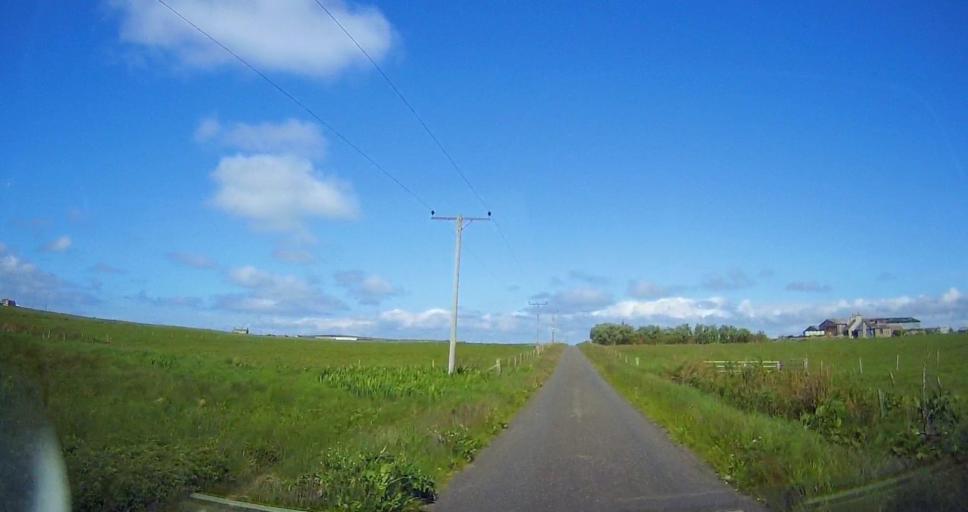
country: GB
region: Scotland
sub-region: Orkney Islands
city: Kirkwall
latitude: 58.8282
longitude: -2.8961
